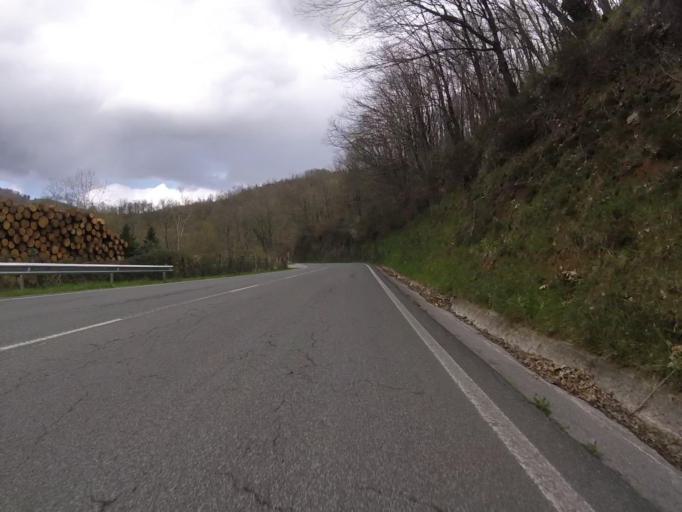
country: ES
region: Navarre
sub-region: Provincia de Navarra
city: Etxalar
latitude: 43.2396
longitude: -1.6656
